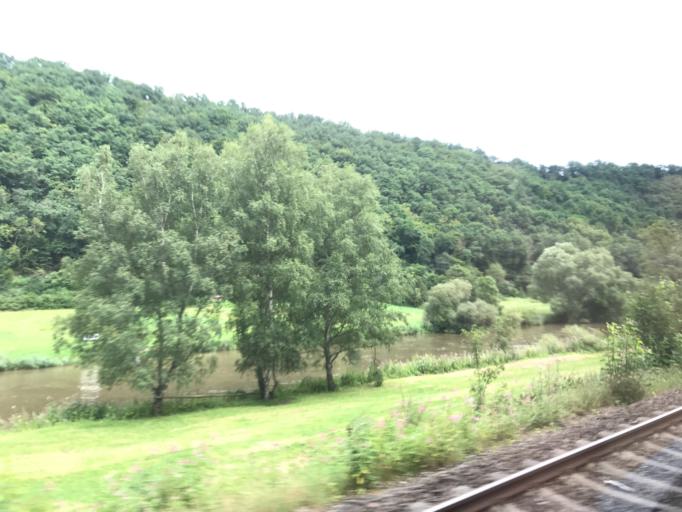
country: DE
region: Rheinland-Pfalz
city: Laurenburg
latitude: 50.3298
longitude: 7.9242
